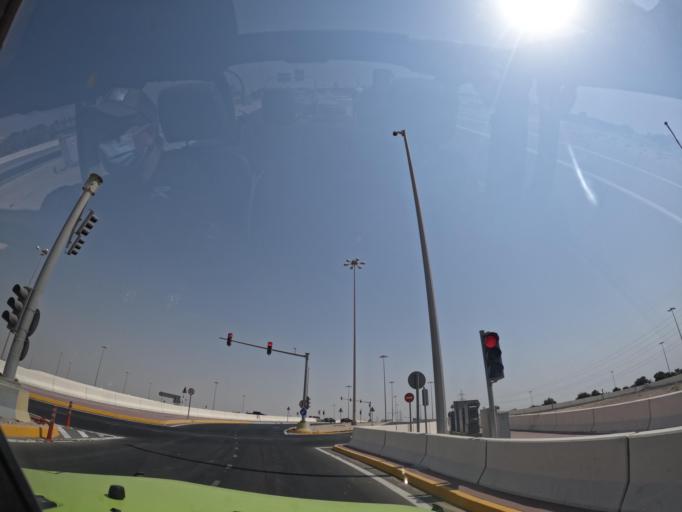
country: AE
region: Abu Dhabi
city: Abu Dhabi
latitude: 24.3284
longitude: 54.6218
